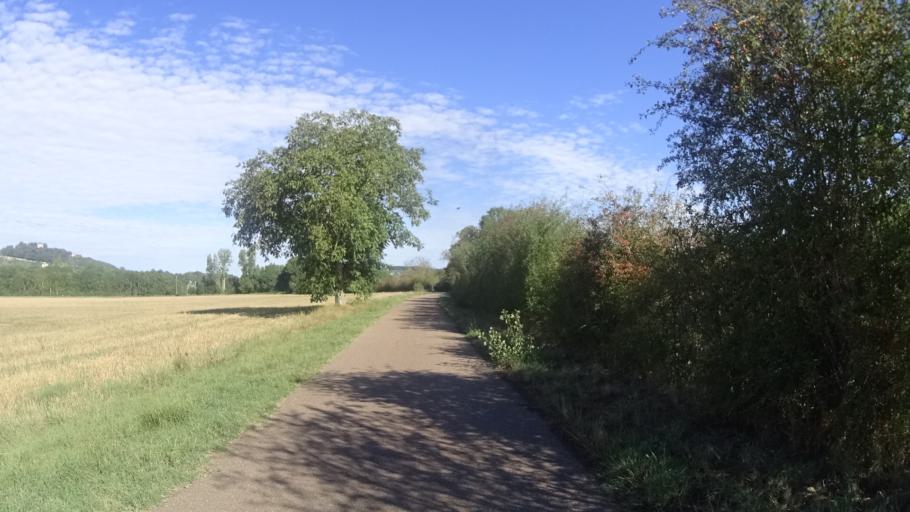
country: FR
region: Centre
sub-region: Departement du Cher
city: Sancerre
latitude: 47.3247
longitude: 2.8662
